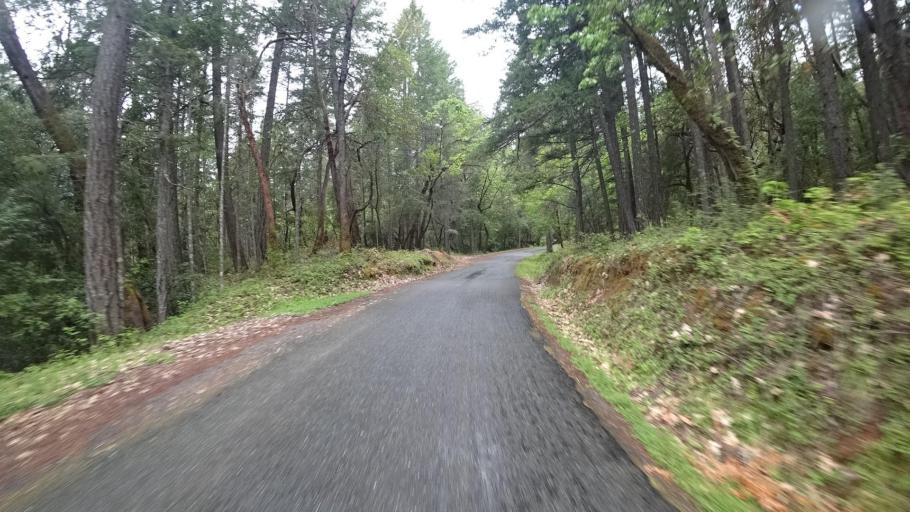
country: US
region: California
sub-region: Humboldt County
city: Willow Creek
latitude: 41.3618
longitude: -123.5061
